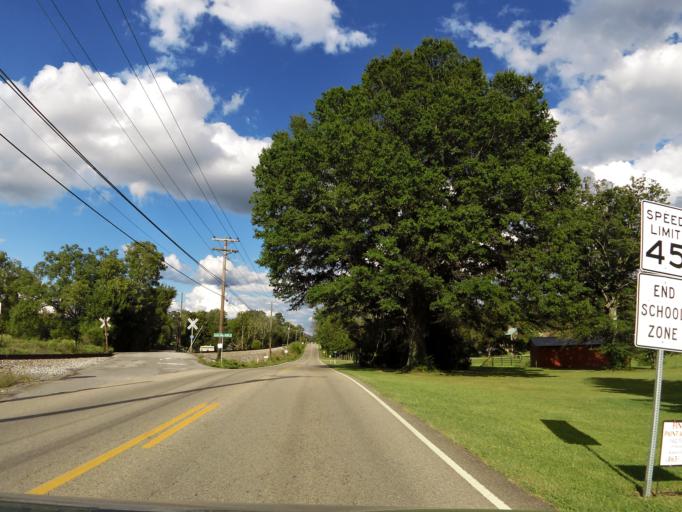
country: US
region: Tennessee
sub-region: Knox County
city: Mascot
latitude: 36.0627
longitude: -83.8582
